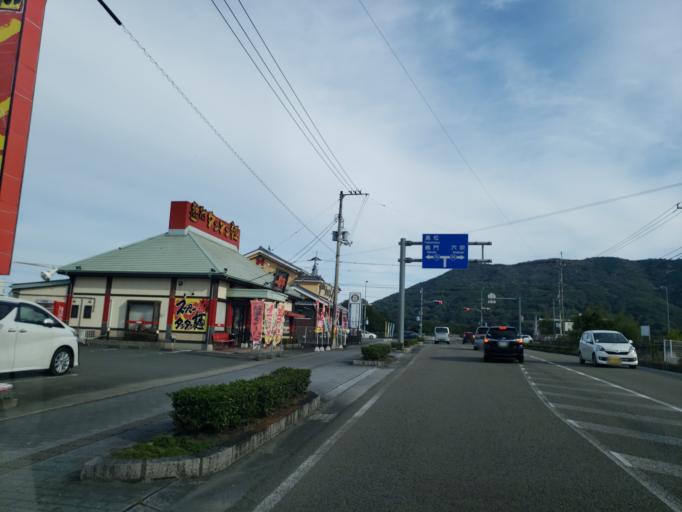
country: JP
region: Tokushima
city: Wakimachi
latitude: 34.0627
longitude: 134.1683
